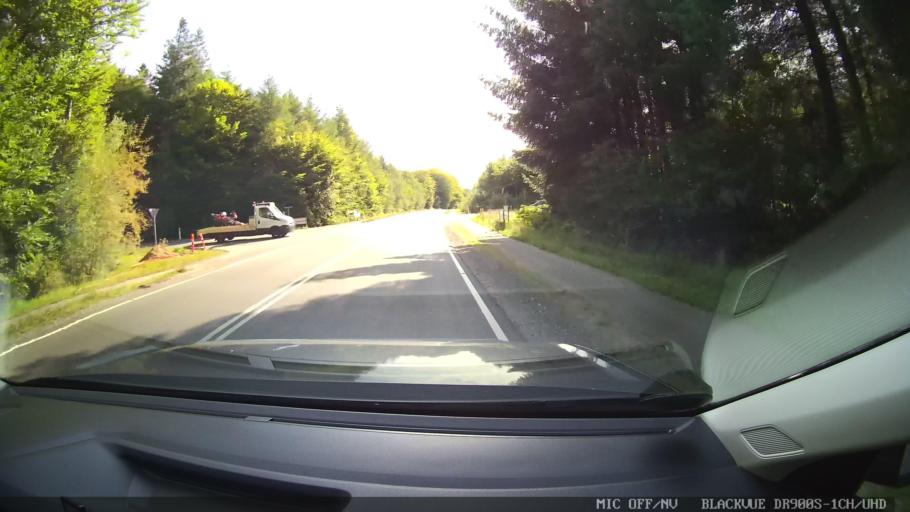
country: DK
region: North Denmark
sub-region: Mariagerfjord Kommune
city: Arden
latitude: 56.7817
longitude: 9.7509
